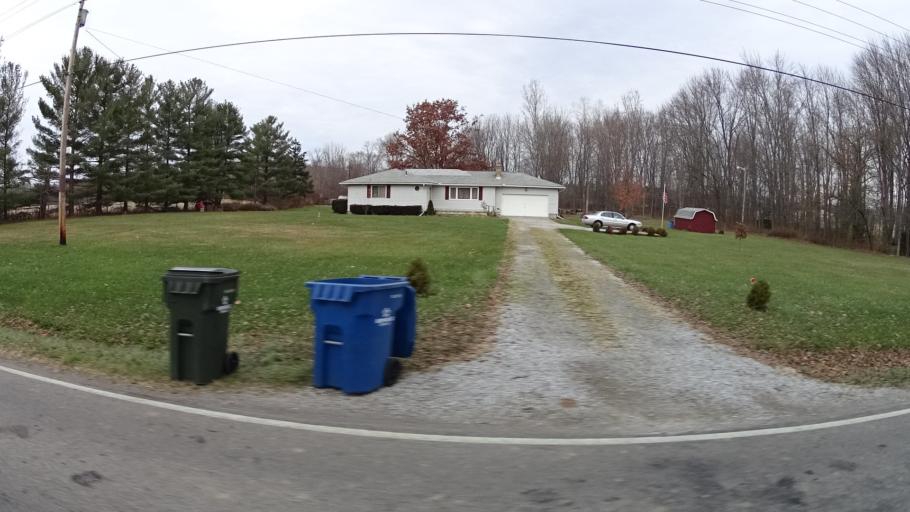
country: US
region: Ohio
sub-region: Lorain County
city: Lagrange
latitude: 41.1998
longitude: -82.1613
